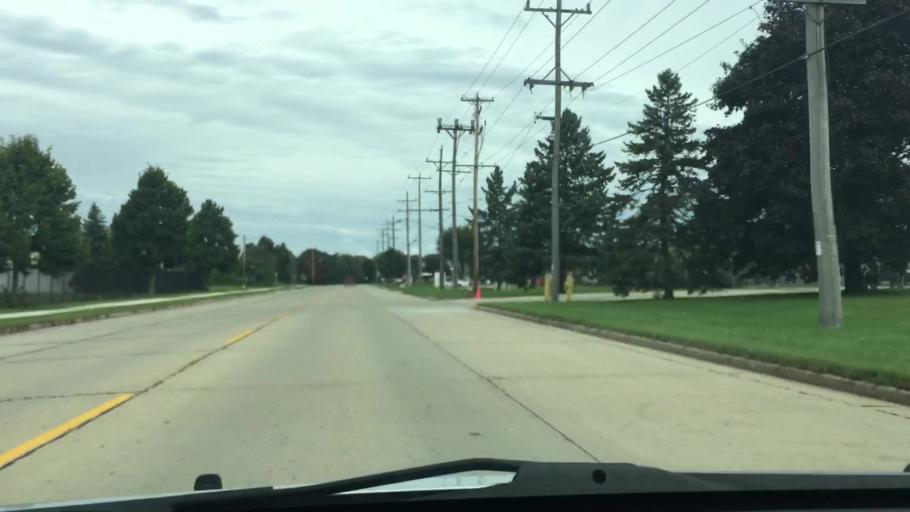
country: US
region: Wisconsin
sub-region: Waukesha County
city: Waukesha
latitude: 42.9988
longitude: -88.2493
